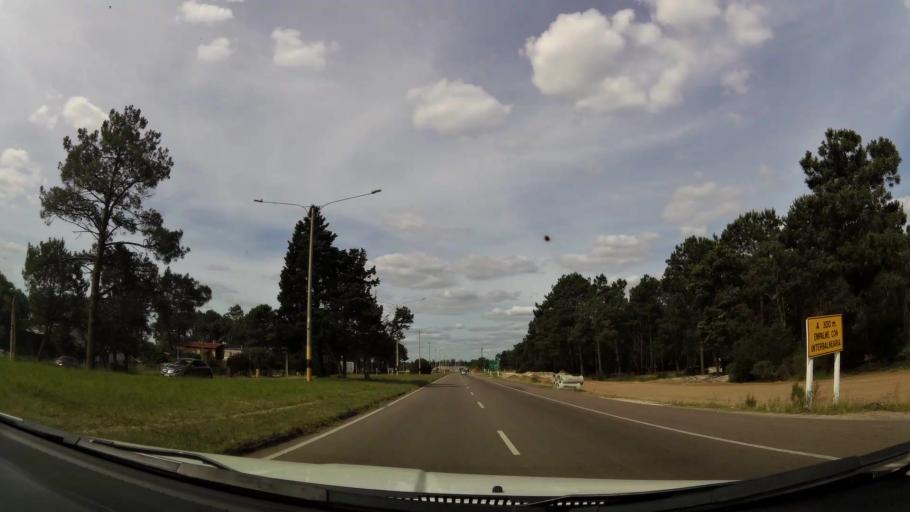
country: UY
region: Canelones
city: Pando
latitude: -34.7912
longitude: -55.8978
